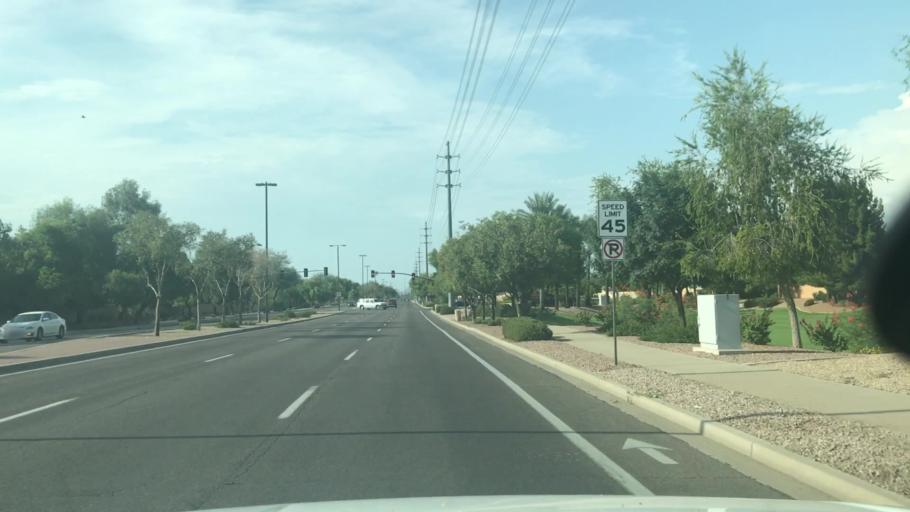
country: US
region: Arizona
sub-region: Maricopa County
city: Gilbert
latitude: 33.3397
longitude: -111.7556
